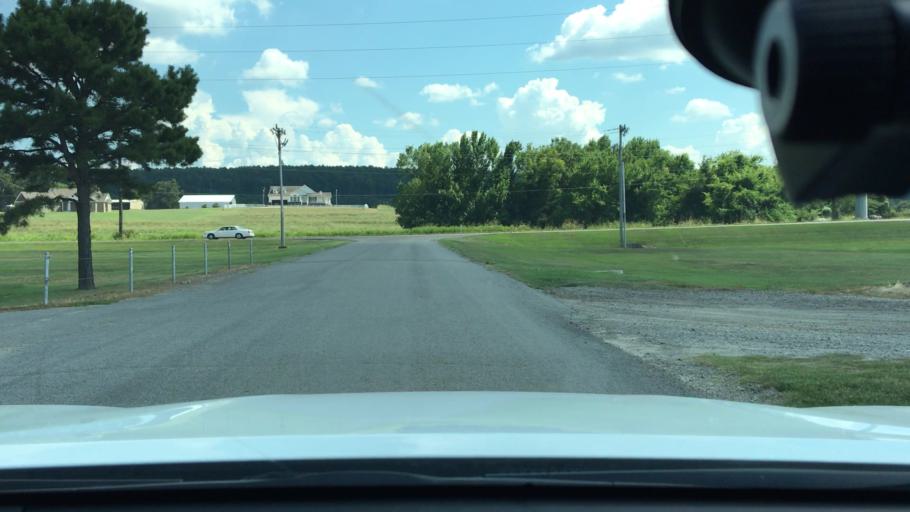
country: US
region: Arkansas
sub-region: Logan County
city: Paris
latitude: 35.2946
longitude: -93.6439
